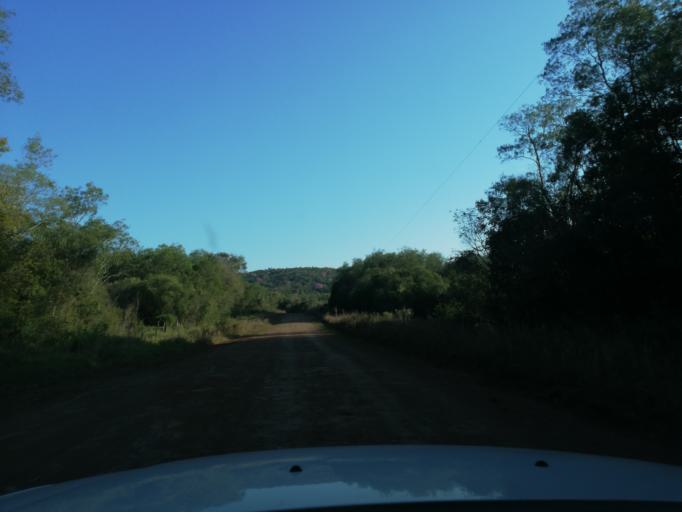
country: AR
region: Misiones
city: Cerro Cora
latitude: -27.6059
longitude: -55.7030
